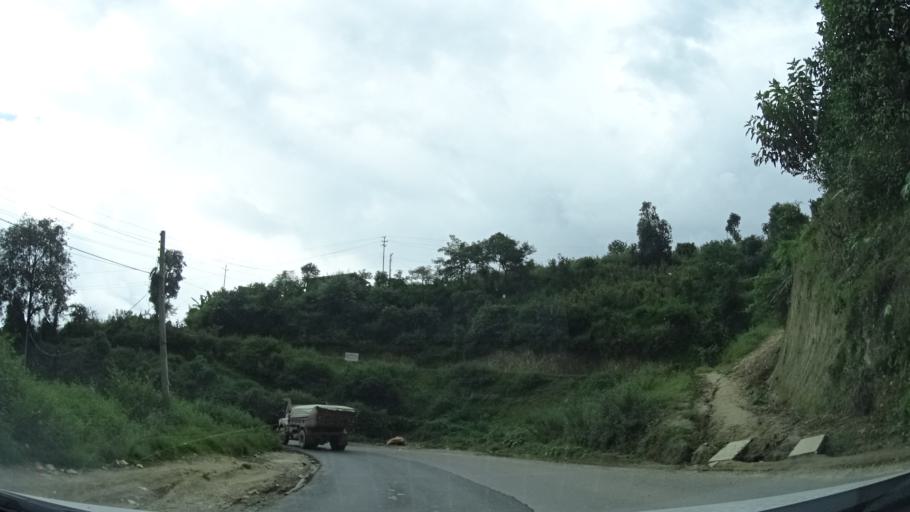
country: NP
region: Central Region
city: Kirtipur
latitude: 27.7189
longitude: 85.1656
